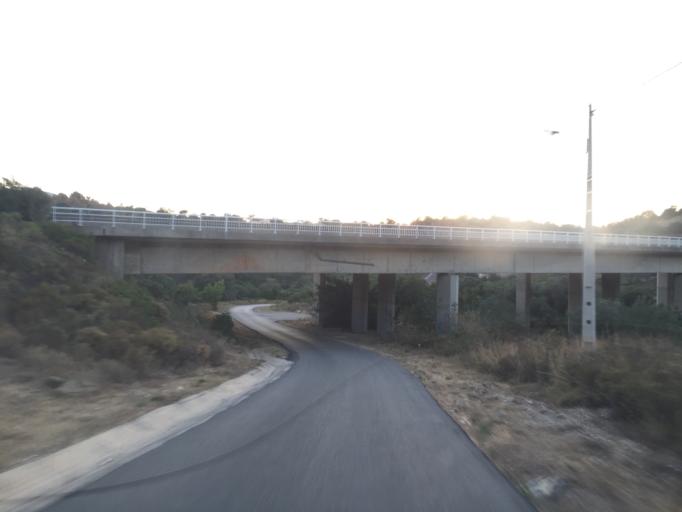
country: PT
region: Faro
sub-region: Loule
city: Almancil
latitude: 37.1034
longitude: -8.0139
